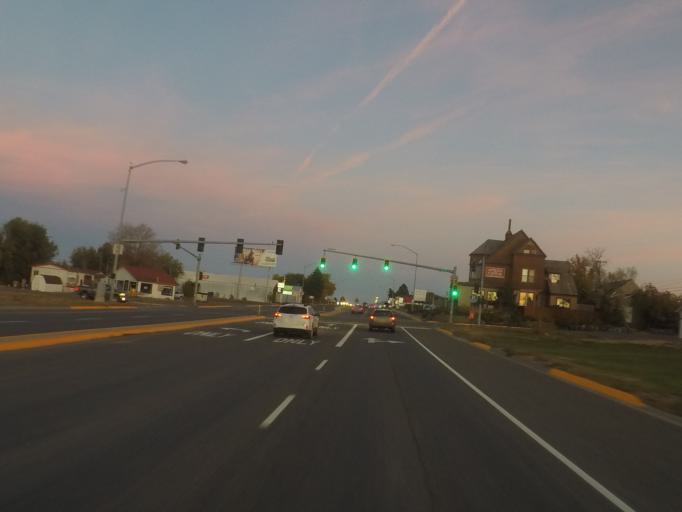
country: US
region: Montana
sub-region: Lewis and Clark County
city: Helena
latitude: 46.6065
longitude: -112.0675
